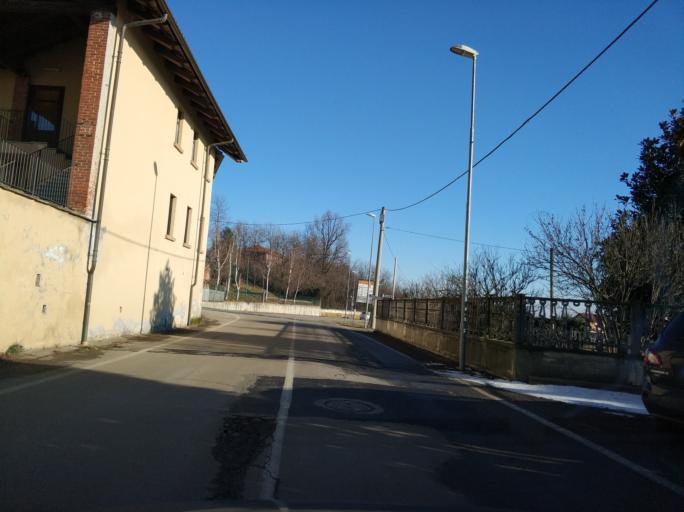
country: IT
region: Piedmont
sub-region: Provincia di Torino
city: San Francesco al Campo
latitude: 45.2240
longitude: 7.6570
